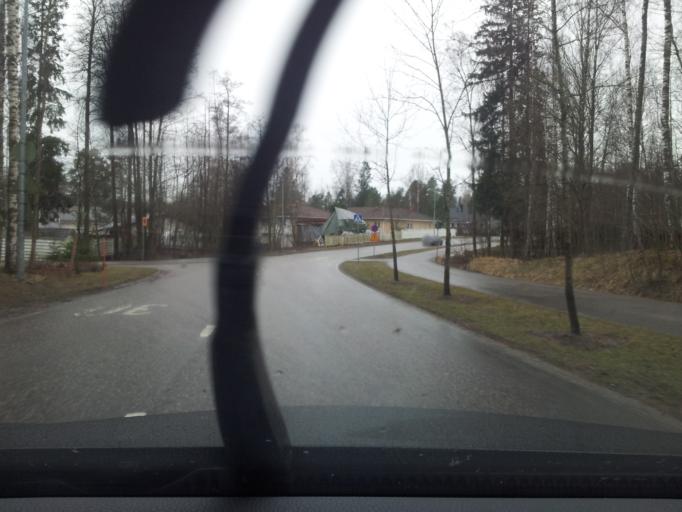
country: FI
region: Uusimaa
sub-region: Helsinki
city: Espoo
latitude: 60.1640
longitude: 24.6811
